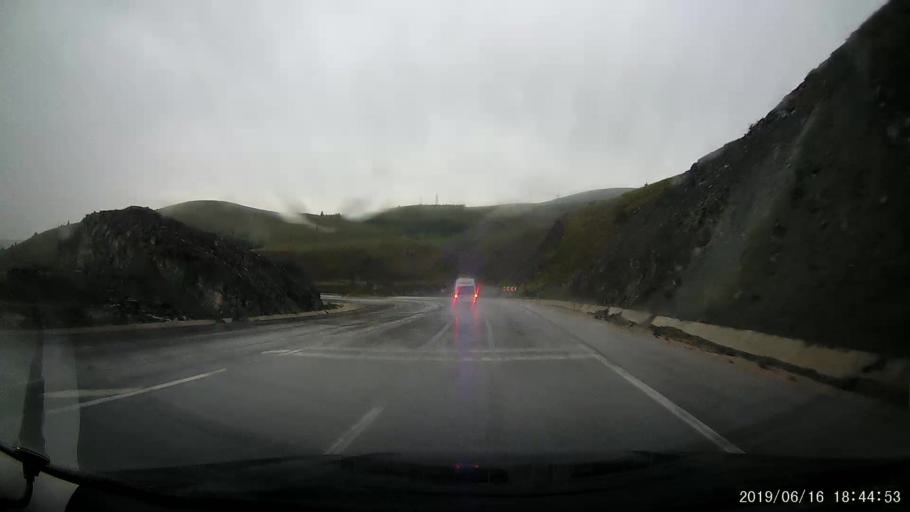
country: TR
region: Erzincan
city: Doganbeyli
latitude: 39.8709
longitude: 39.0659
